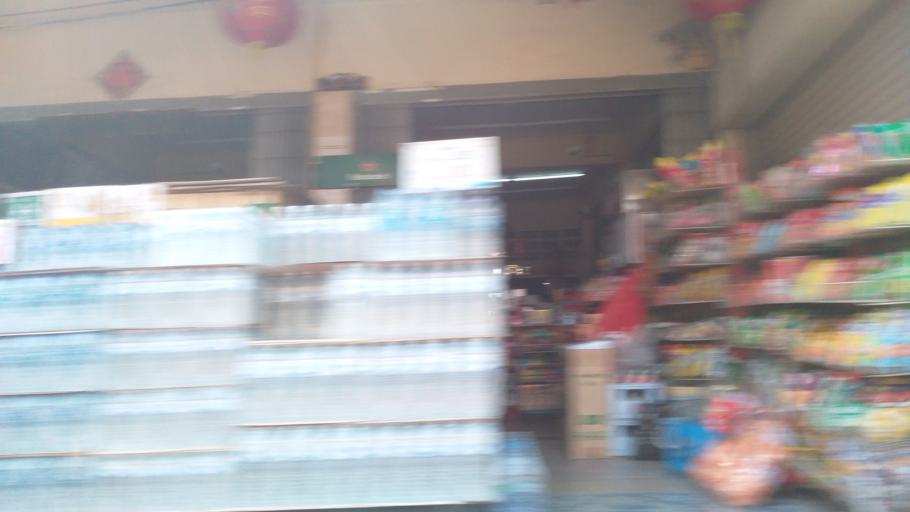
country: TH
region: Khon Kaen
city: Khon Kaen
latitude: 16.4342
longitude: 102.8314
